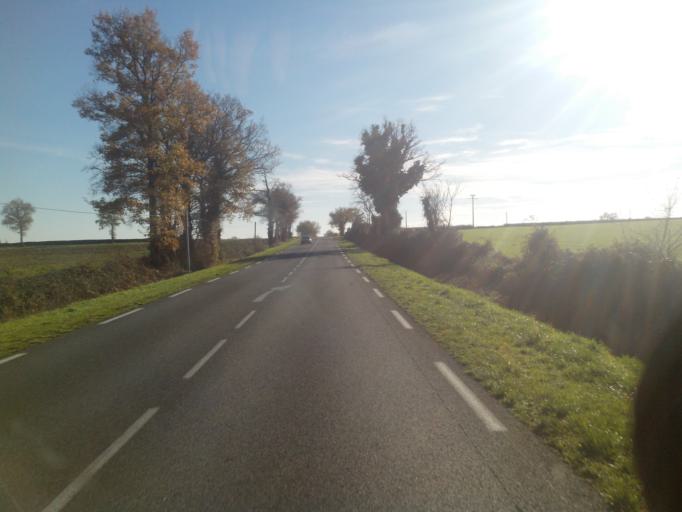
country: FR
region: Poitou-Charentes
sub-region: Departement de la Vienne
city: Saulge
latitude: 46.2991
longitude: 0.8389
